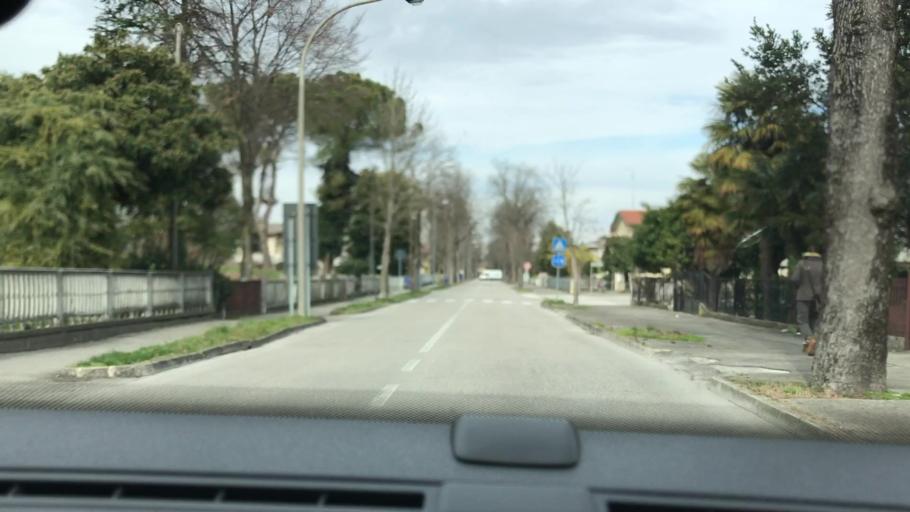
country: IT
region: Veneto
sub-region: Provincia di Venezia
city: Santo Stino di Livenza
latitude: 45.7218
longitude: 12.6813
